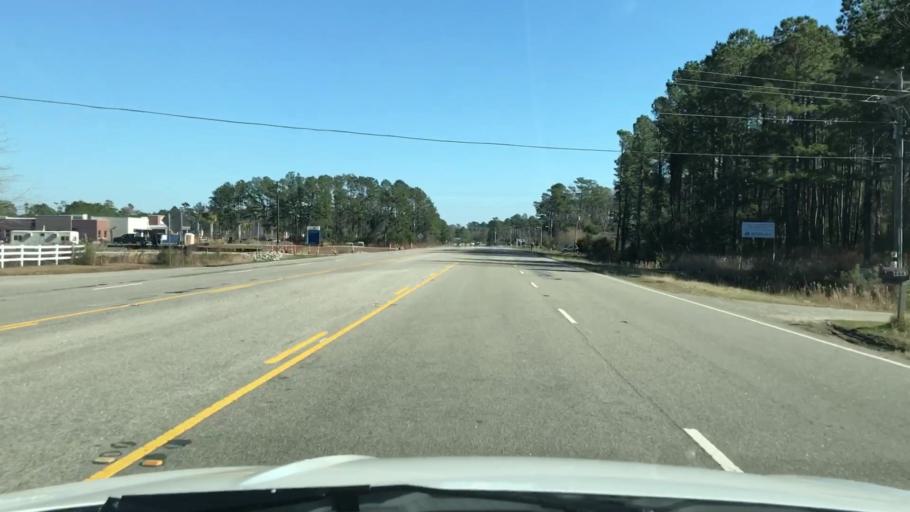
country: US
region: South Carolina
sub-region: Horry County
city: Garden City
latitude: 33.6298
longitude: -79.0290
